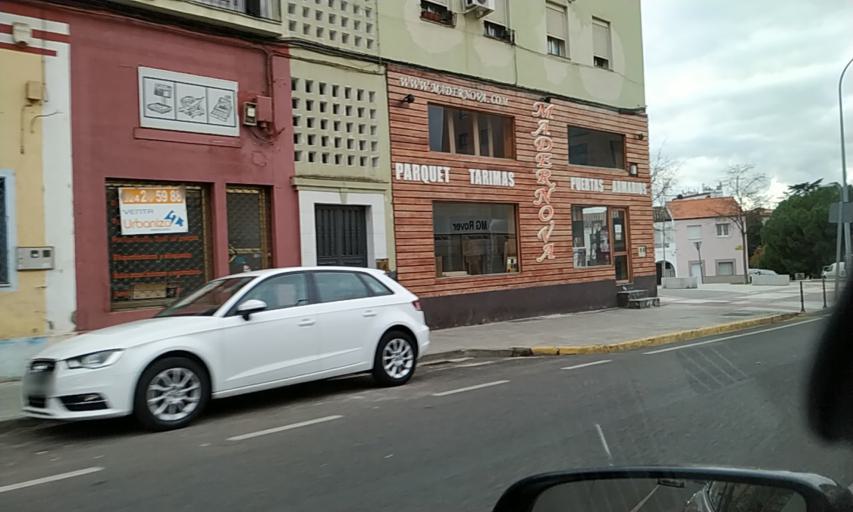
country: ES
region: Extremadura
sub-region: Provincia de Badajoz
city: Badajoz
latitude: 38.8774
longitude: -6.9606
